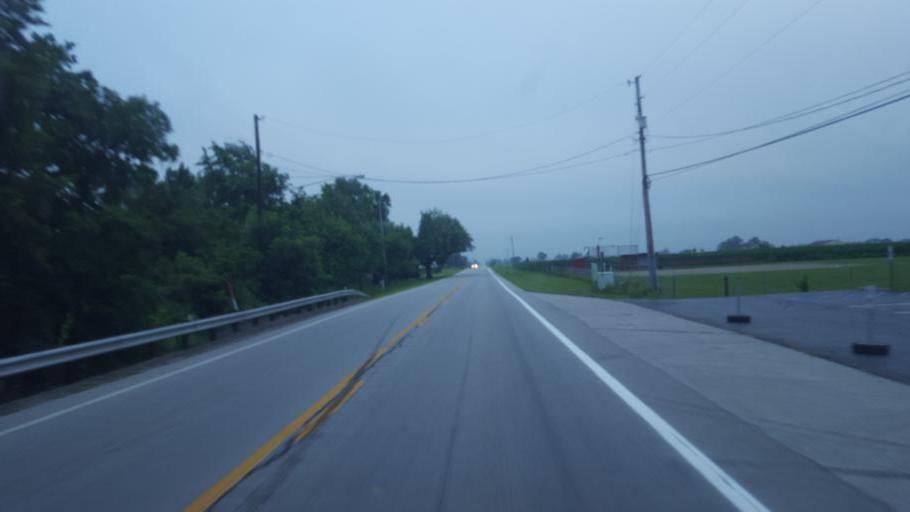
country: US
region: Ohio
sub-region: Madison County
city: Mount Sterling
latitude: 39.6490
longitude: -83.3318
